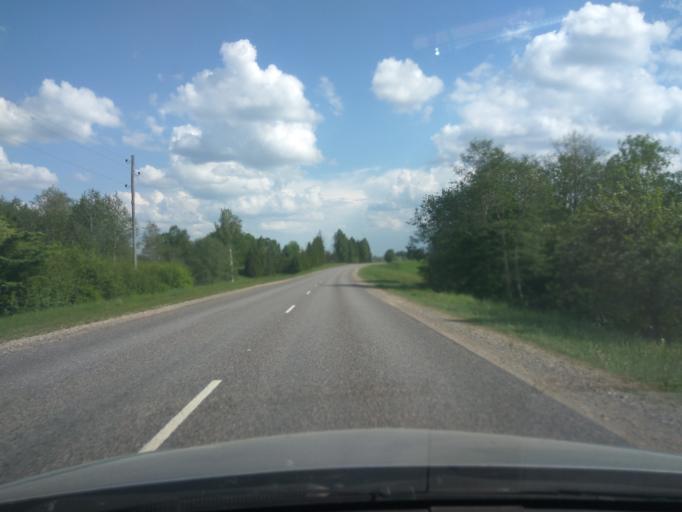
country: LV
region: Kuldigas Rajons
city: Kuldiga
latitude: 57.0196
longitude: 21.8715
